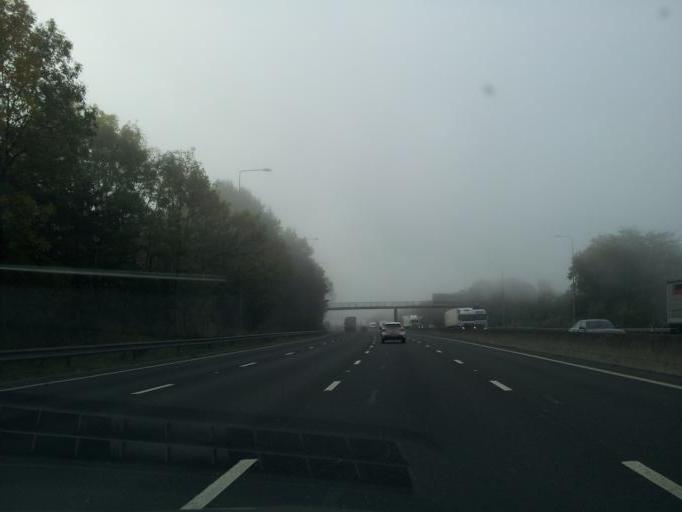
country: GB
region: England
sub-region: Kirklees
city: Cleckheaton
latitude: 53.7149
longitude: -1.7456
